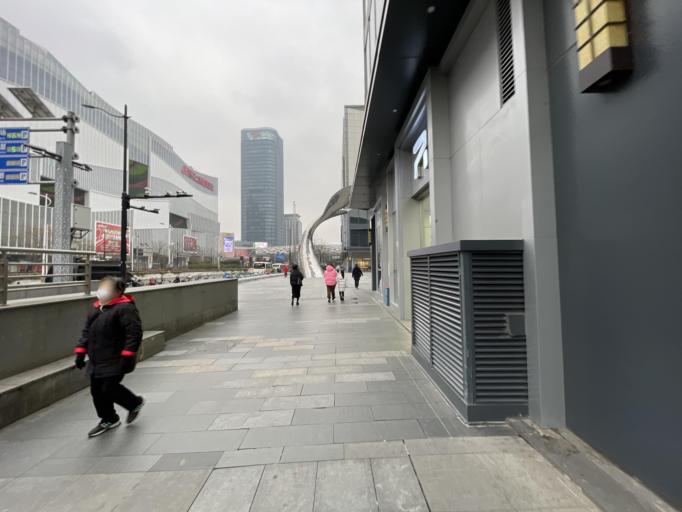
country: CN
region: Shanghai Shi
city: Yangpu
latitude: 31.3039
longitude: 121.5099
